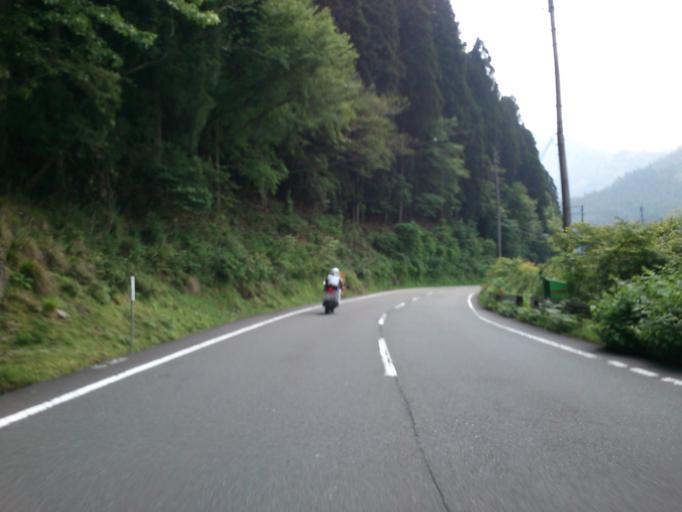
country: JP
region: Kyoto
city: Kameoka
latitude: 35.2572
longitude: 135.5687
